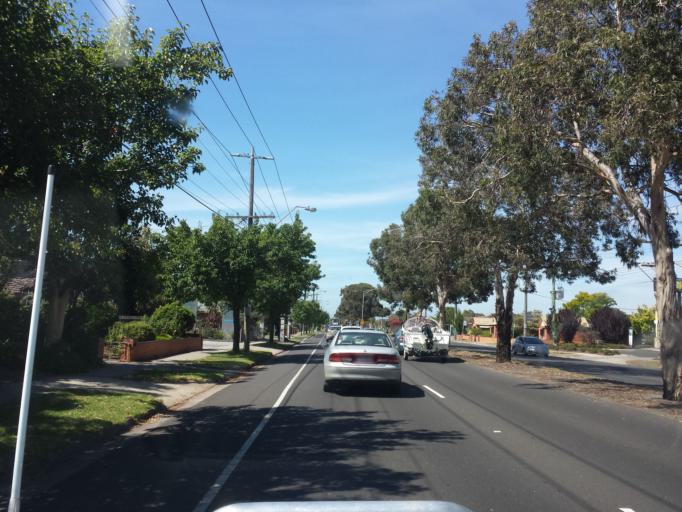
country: AU
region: Victoria
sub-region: Hobsons Bay
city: Altona North
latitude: -37.8323
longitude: 144.8481
